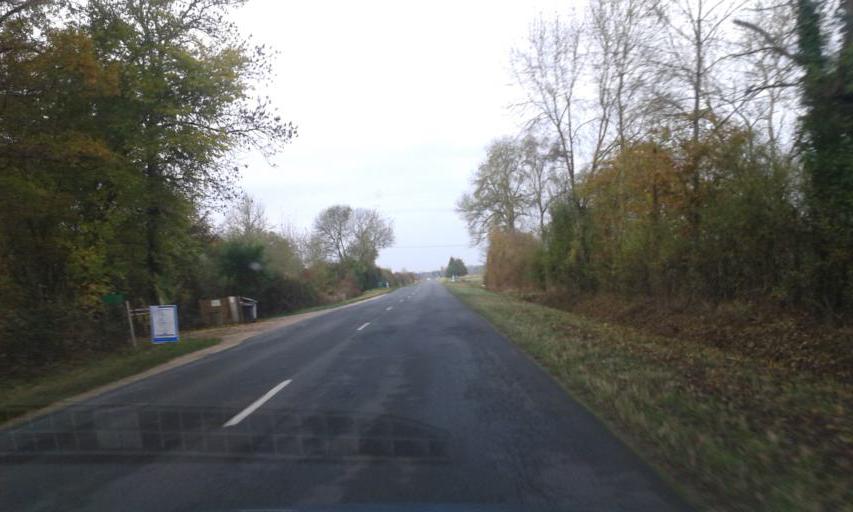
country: FR
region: Centre
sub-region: Departement du Loiret
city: Lailly-en-Val
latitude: 47.7734
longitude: 1.6814
